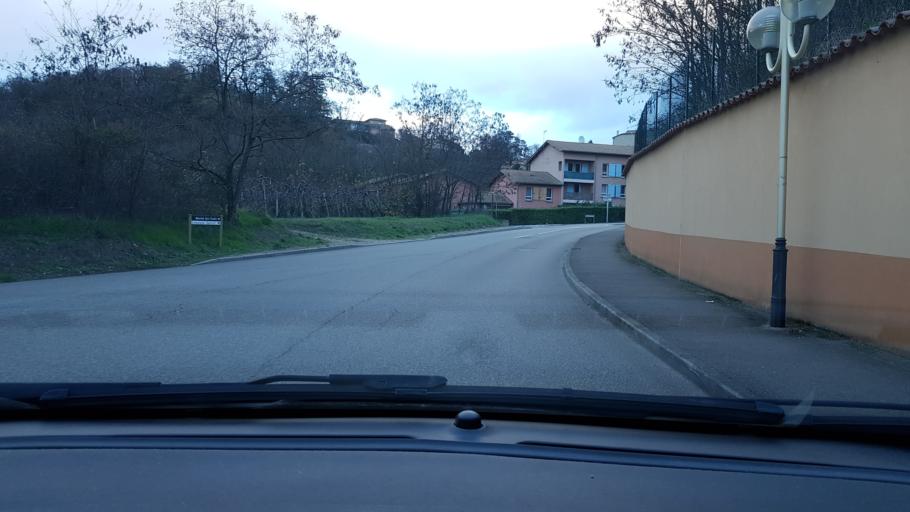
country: FR
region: Rhone-Alpes
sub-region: Departement du Rhone
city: Vourles
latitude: 45.6580
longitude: 4.7687
